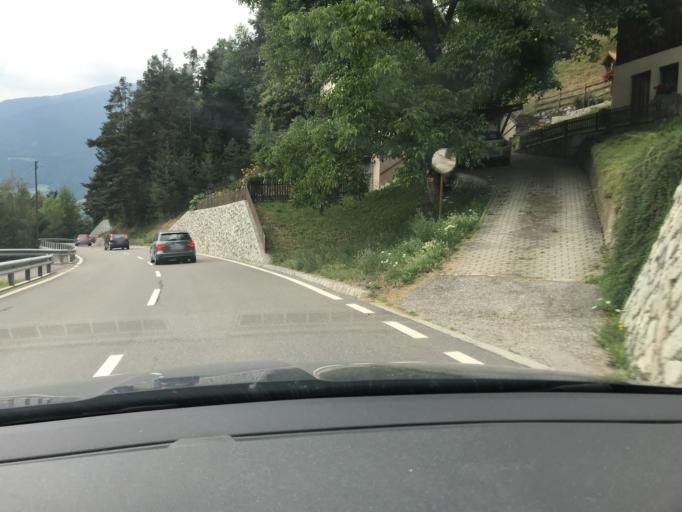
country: IT
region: Trentino-Alto Adige
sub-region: Bolzano
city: Bressanone
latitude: 46.6959
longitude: 11.6810
